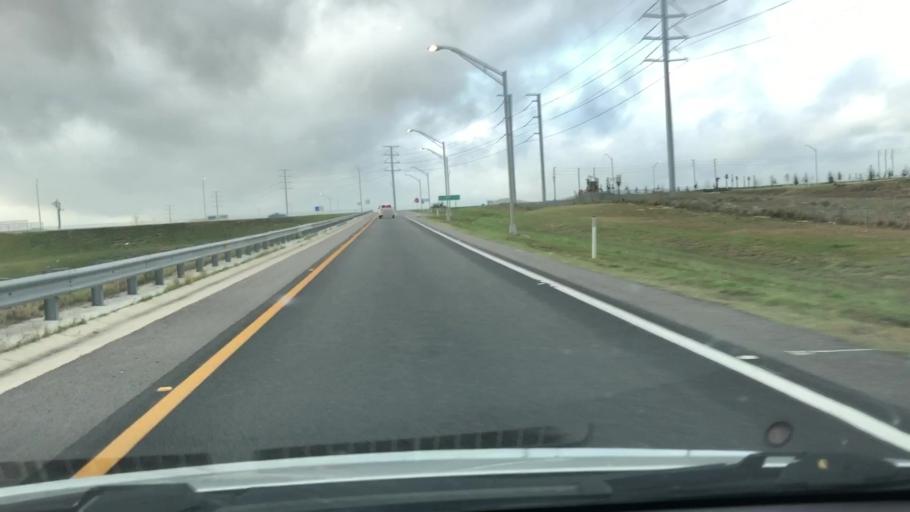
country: US
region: Florida
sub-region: Orange County
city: Oakland
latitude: 28.4766
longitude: -81.6323
